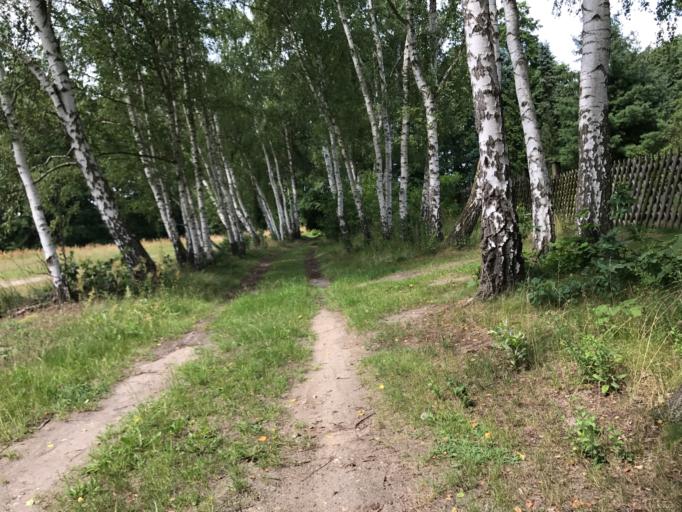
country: DE
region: Brandenburg
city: Wandlitz
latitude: 52.7488
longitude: 13.4406
